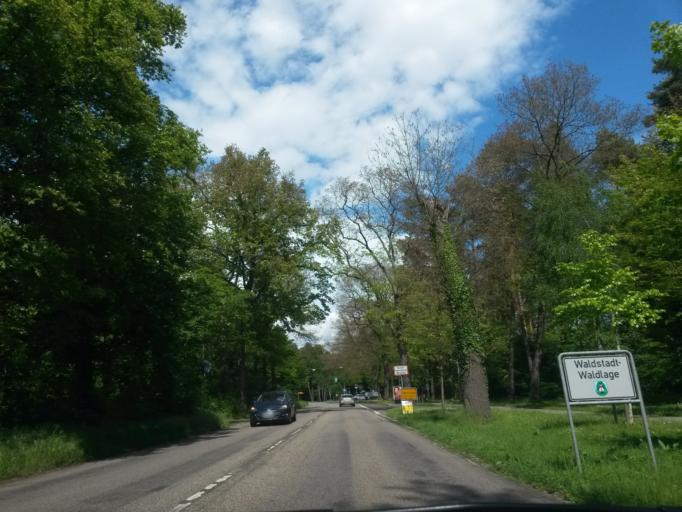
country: DE
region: Baden-Wuerttemberg
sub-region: Karlsruhe Region
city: Karlsruhe
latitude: 49.0282
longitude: 8.4292
